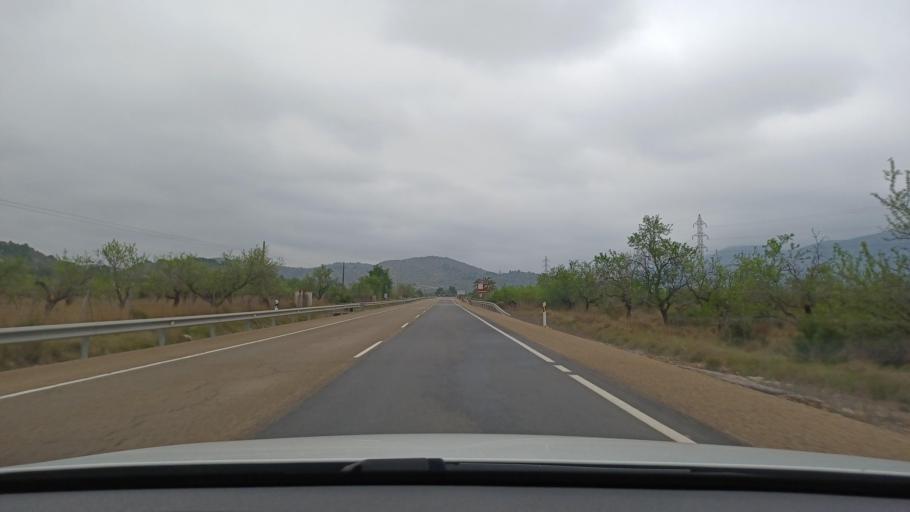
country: ES
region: Valencia
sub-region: Provincia de Castello
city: Alcala de Xivert
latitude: 40.2586
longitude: 0.2377
